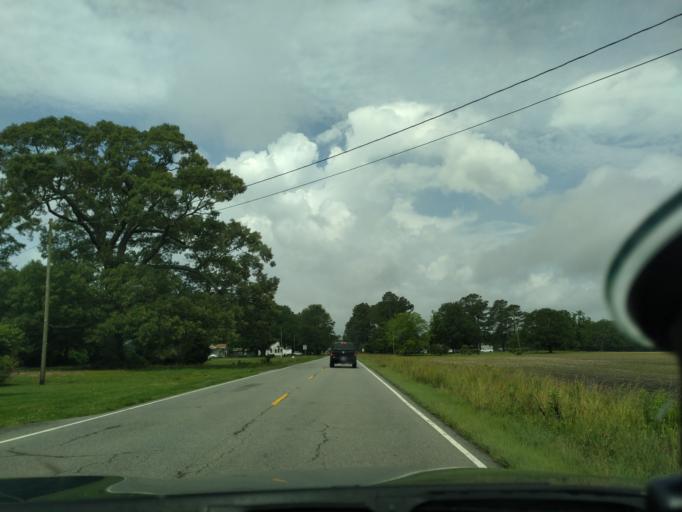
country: US
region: North Carolina
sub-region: Washington County
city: Plymouth
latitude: 35.8764
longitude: -76.6527
